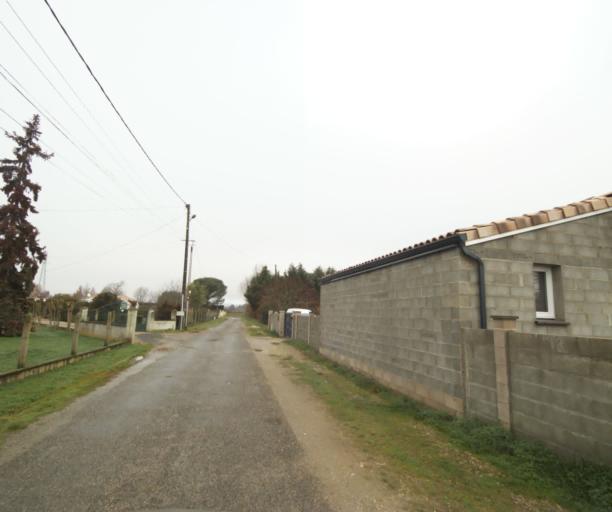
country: FR
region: Midi-Pyrenees
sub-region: Departement de la Haute-Garonne
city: Villemur-sur-Tarn
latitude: 43.8561
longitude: 1.4644
